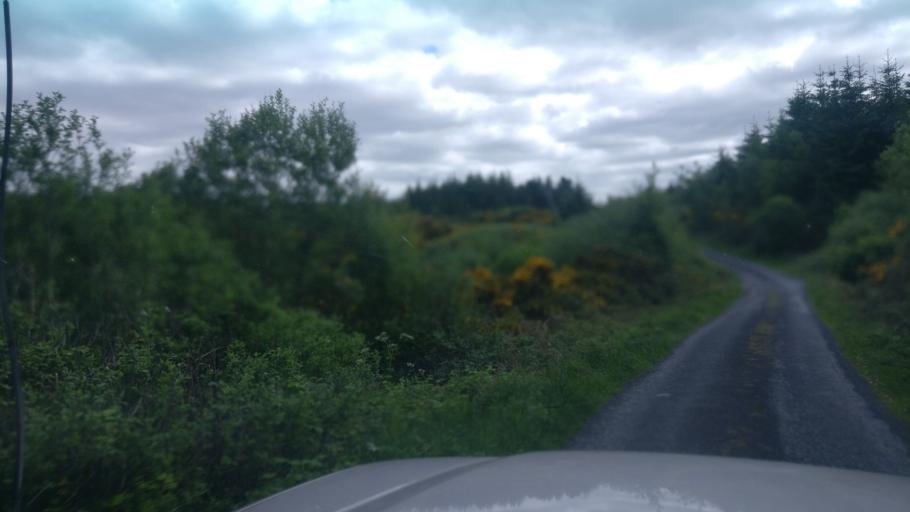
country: IE
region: Connaught
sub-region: County Galway
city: Gort
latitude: 53.1189
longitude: -8.6876
